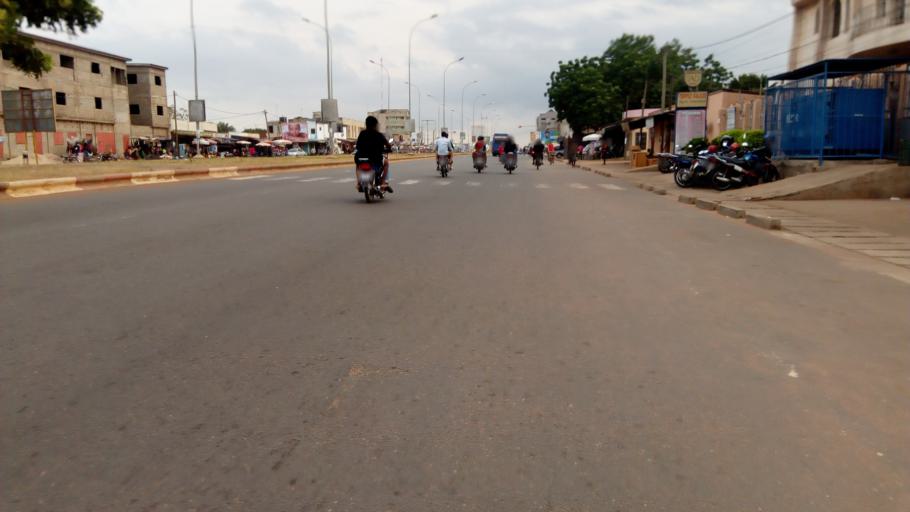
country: TG
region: Maritime
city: Lome
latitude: 6.2344
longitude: 1.1992
